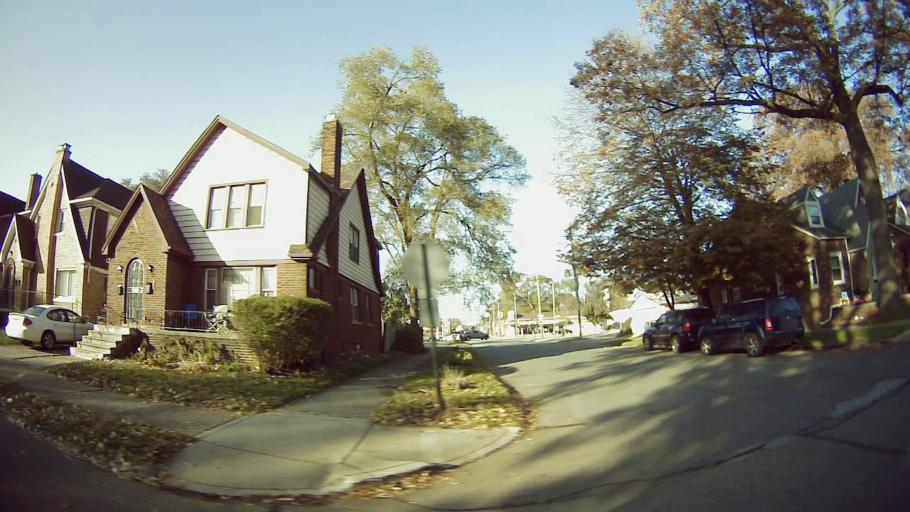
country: US
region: Michigan
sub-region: Oakland County
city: Ferndale
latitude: 42.4190
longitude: -83.1401
